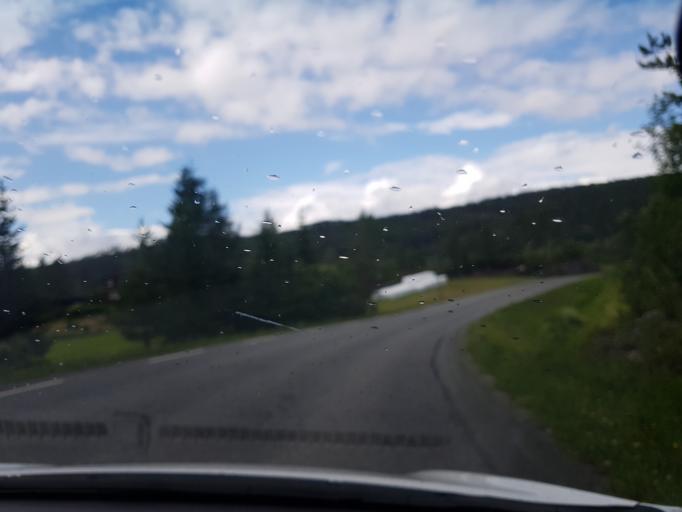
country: NO
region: Nord-Trondelag
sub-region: Stjordal
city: Stjordalshalsen
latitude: 63.6092
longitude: 10.9365
